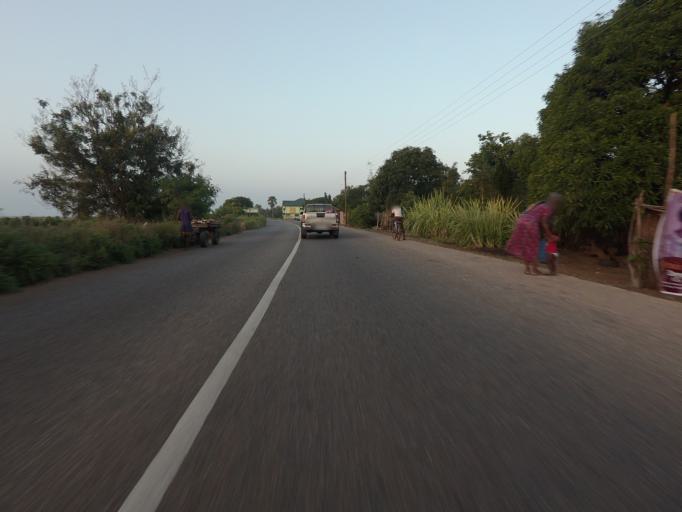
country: GH
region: Volta
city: Anloga
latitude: 5.8125
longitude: 0.9359
